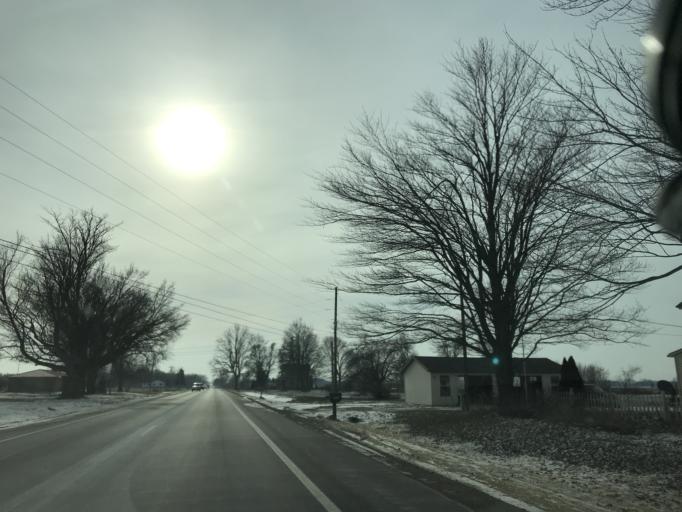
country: US
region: Michigan
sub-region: Ionia County
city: Lake Odessa
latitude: 42.8640
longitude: -85.0750
